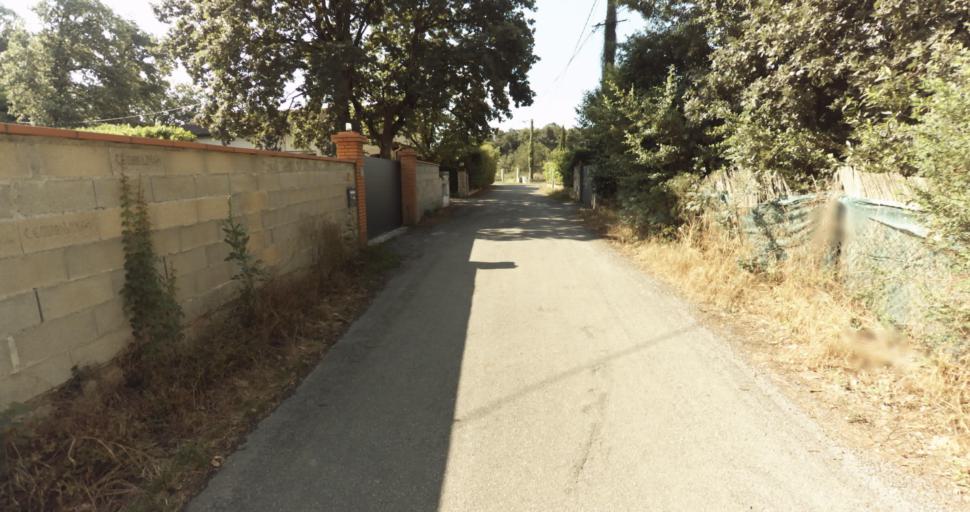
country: FR
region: Midi-Pyrenees
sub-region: Departement de la Haute-Garonne
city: Fontenilles
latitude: 43.5612
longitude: 1.2176
